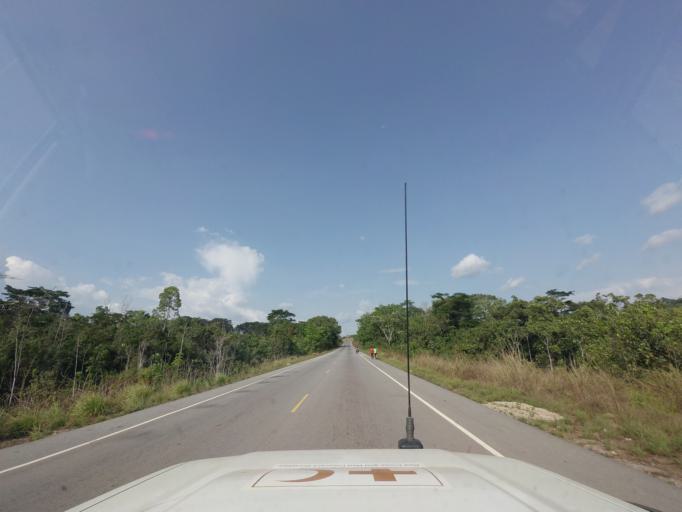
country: LR
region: Bong
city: Gbarnga
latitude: 6.8179
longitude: -9.8925
